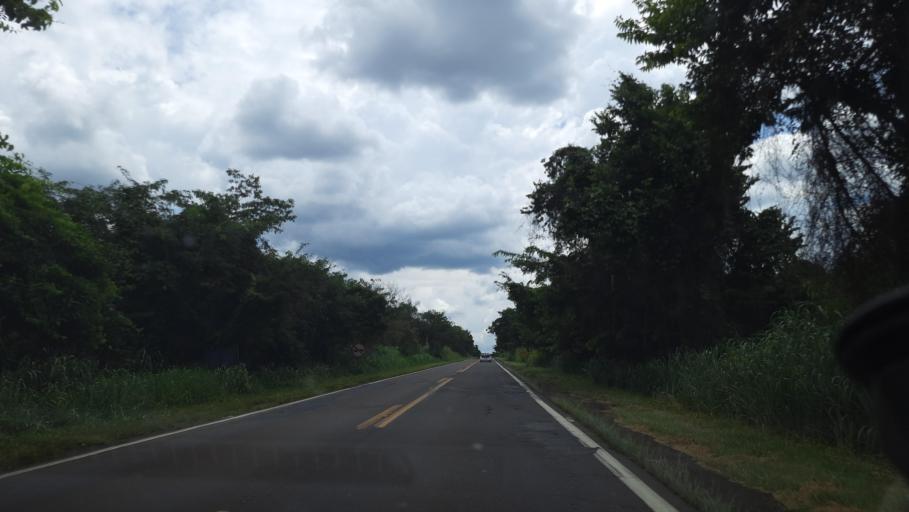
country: BR
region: Sao Paulo
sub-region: Mococa
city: Mococa
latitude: -21.4611
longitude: -47.1102
